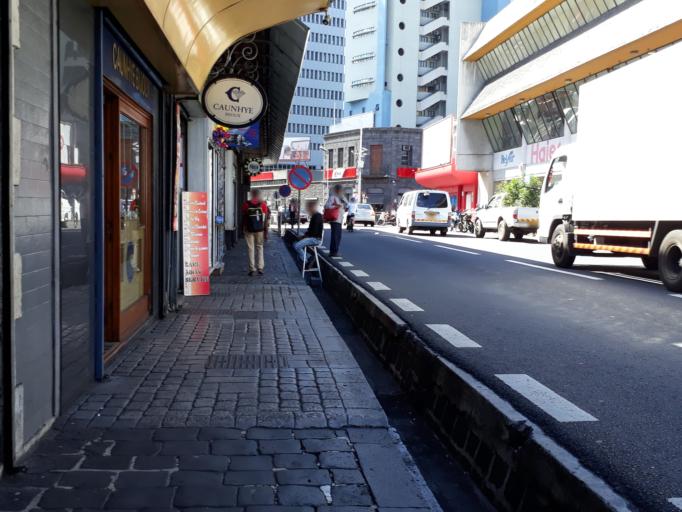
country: MU
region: Port Louis
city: Port Louis
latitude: -20.1636
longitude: 57.4991
